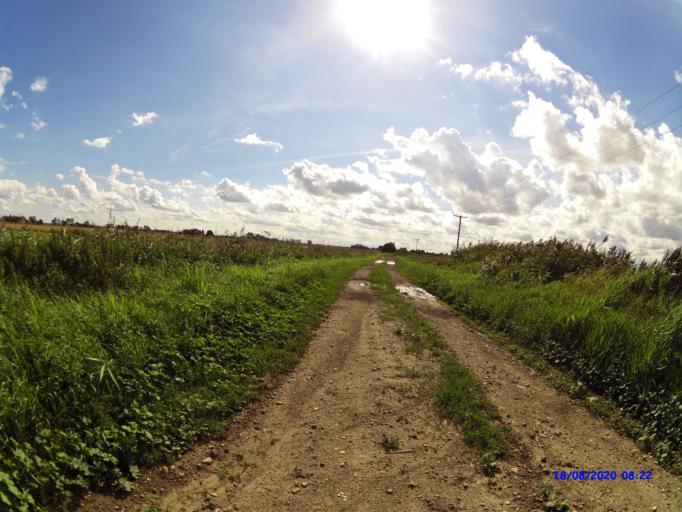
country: GB
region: England
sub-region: Cambridgeshire
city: Ramsey
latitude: 52.5034
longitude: -0.0756
